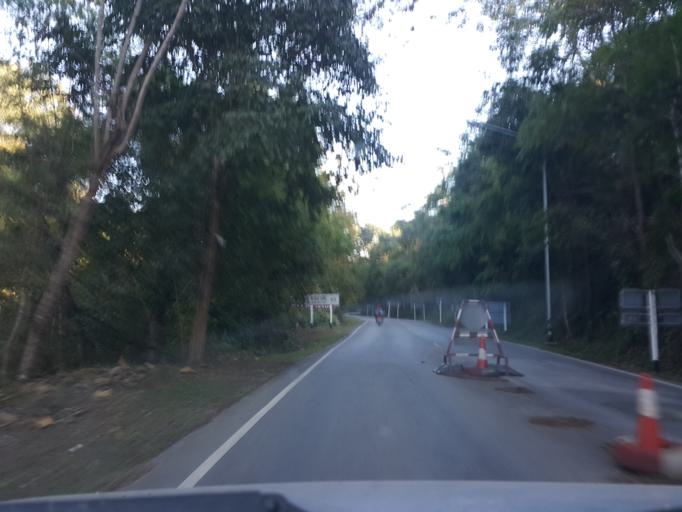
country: TH
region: Mae Hong Son
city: Mae Hi
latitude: 19.2853
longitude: 98.4840
